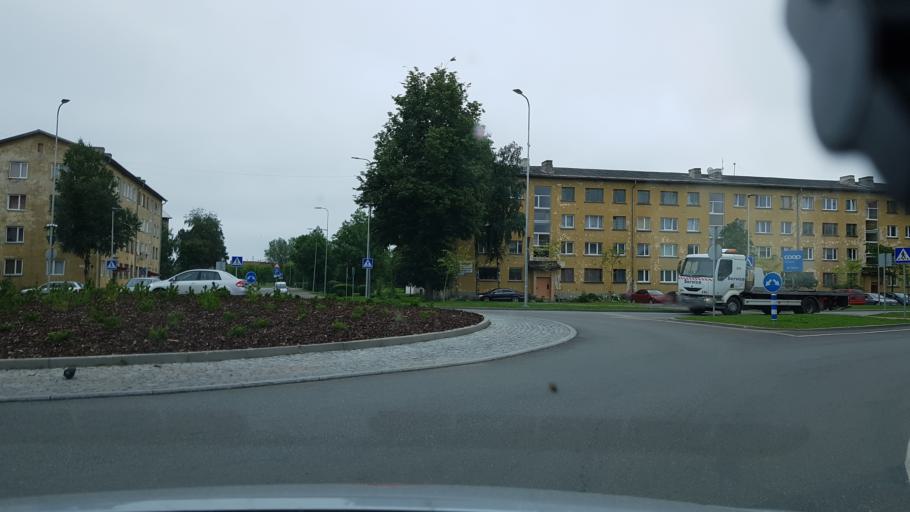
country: EE
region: Ida-Virumaa
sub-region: Kohtla-Jaerve linn
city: Kohtla-Jarve
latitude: 59.4006
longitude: 27.2891
